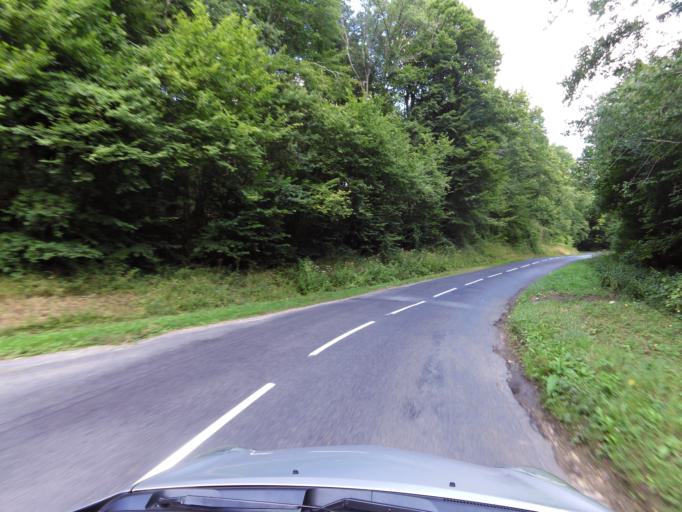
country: FR
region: Picardie
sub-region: Departement de l'Aisne
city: Neuilly-Saint-Front
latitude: 49.2612
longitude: 3.2162
